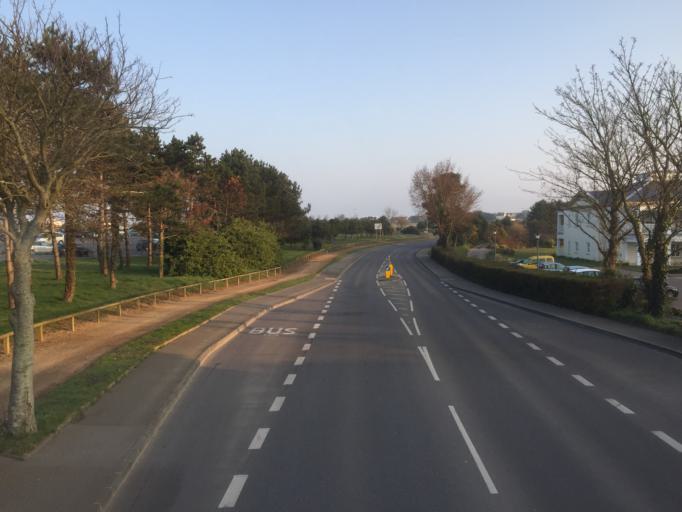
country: JE
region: St Helier
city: Saint Helier
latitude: 49.2045
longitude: -2.1898
